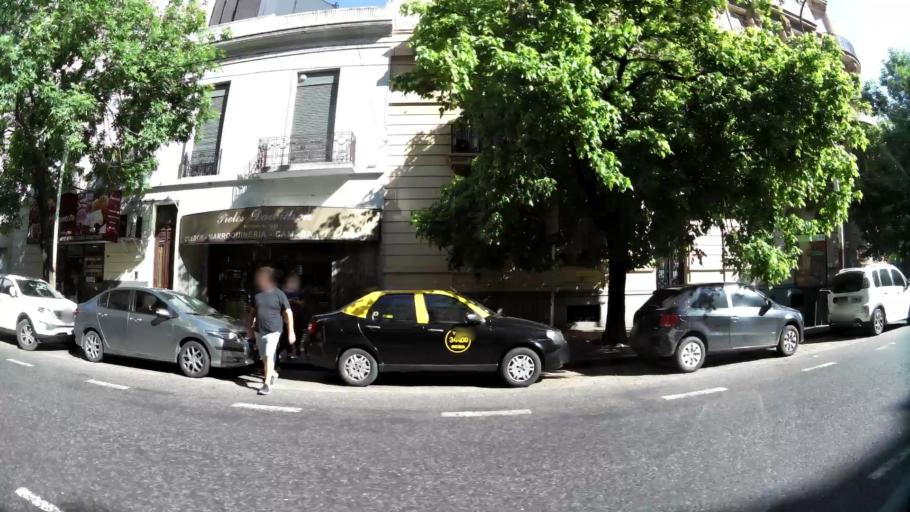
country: AR
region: Buenos Aires F.D.
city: Colegiales
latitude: -34.6149
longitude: -58.4282
